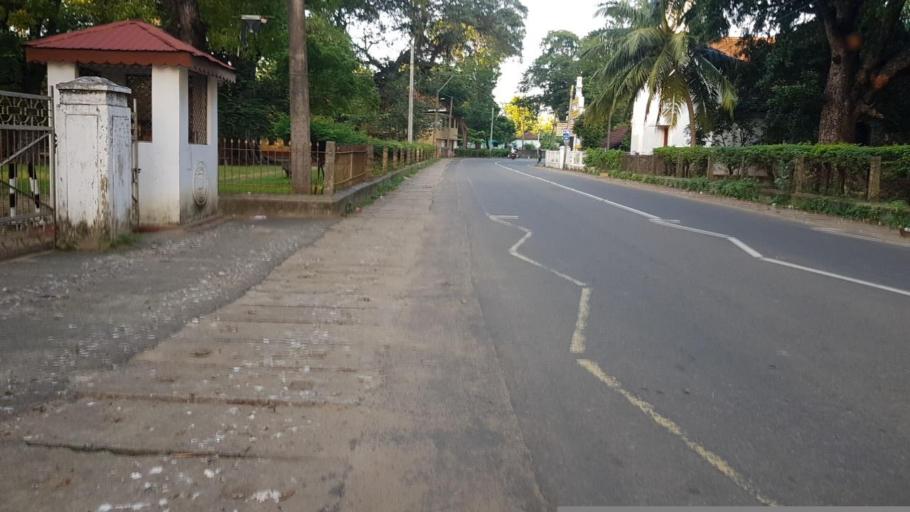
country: LK
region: Northern Province
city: Jaffna
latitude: 9.7291
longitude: 79.9487
